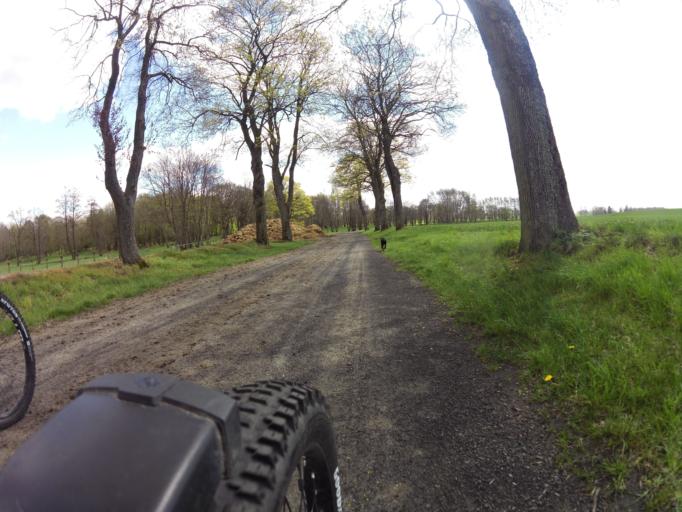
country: PL
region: West Pomeranian Voivodeship
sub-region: Powiat gryficki
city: Gryfice
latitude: 53.8488
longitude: 15.1722
